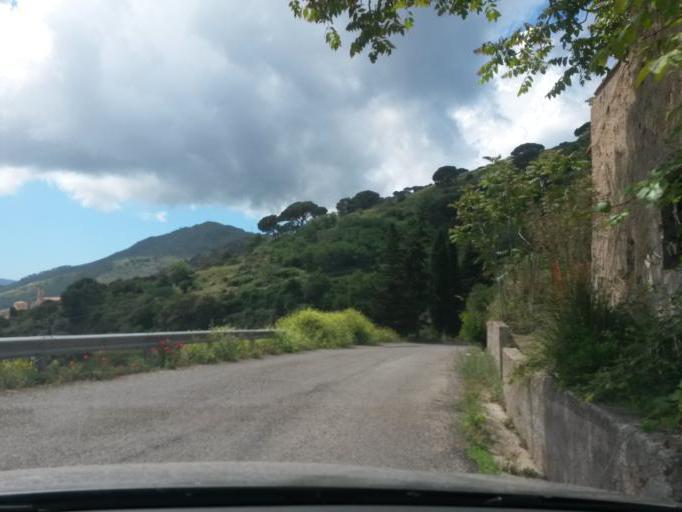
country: IT
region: Tuscany
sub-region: Provincia di Livorno
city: Rio nell'Elba
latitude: 42.8190
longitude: 10.4024
